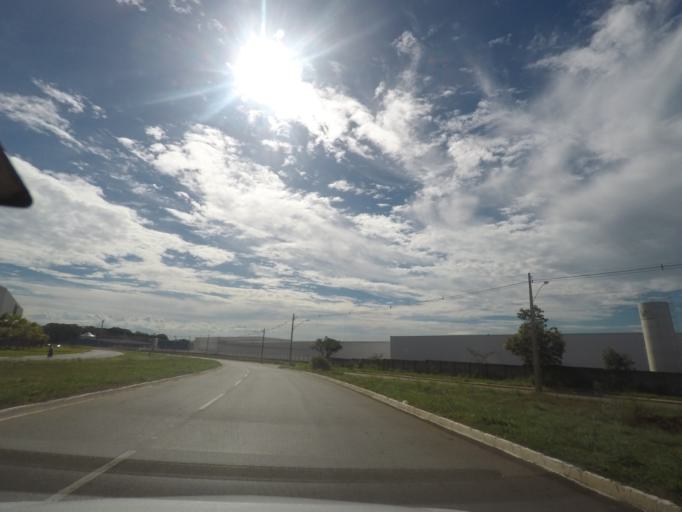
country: BR
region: Goias
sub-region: Aparecida De Goiania
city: Aparecida de Goiania
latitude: -16.8092
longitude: -49.2681
